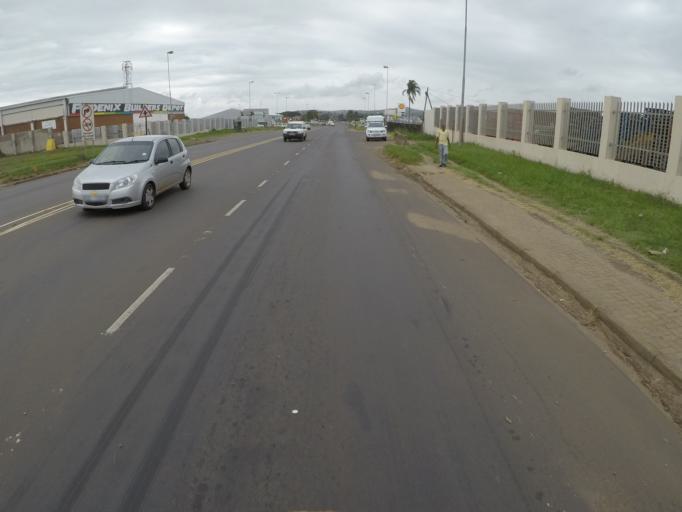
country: ZA
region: KwaZulu-Natal
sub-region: uThungulu District Municipality
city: Empangeni
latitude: -28.7784
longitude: 31.8989
